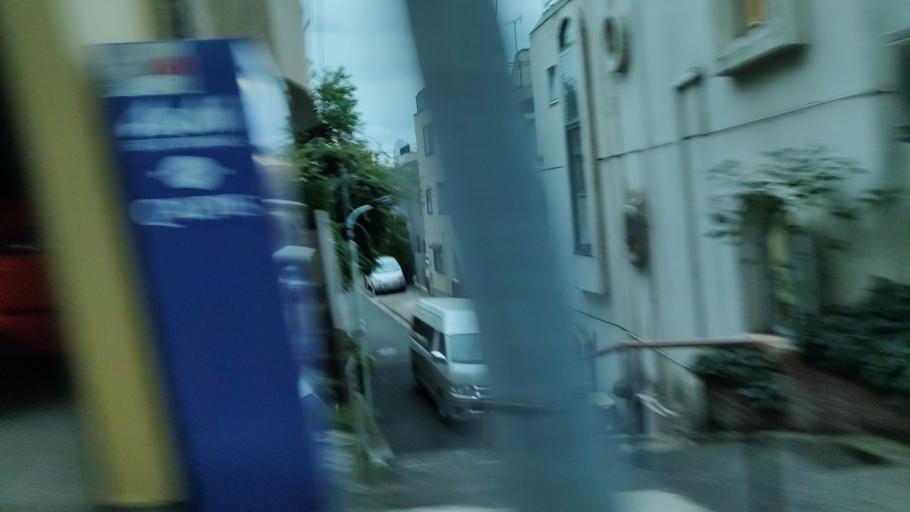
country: JP
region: Tokyo
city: Tokyo
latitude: 35.6480
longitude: 139.7285
